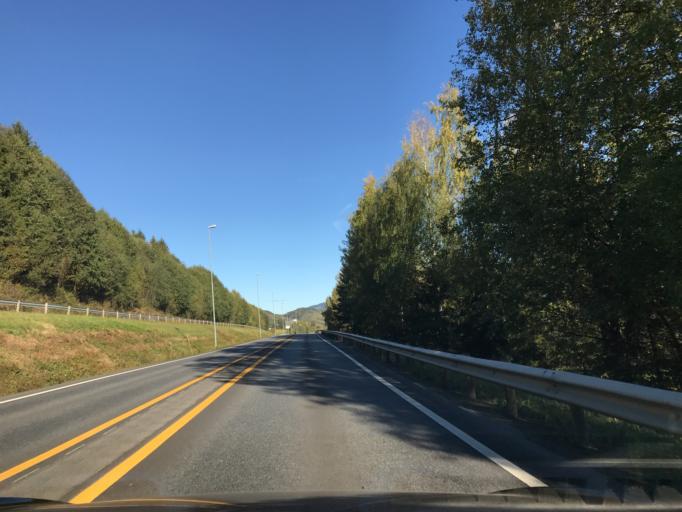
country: NO
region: Oppland
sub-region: Lillehammer
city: Lillehammer
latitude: 61.0623
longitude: 10.4308
